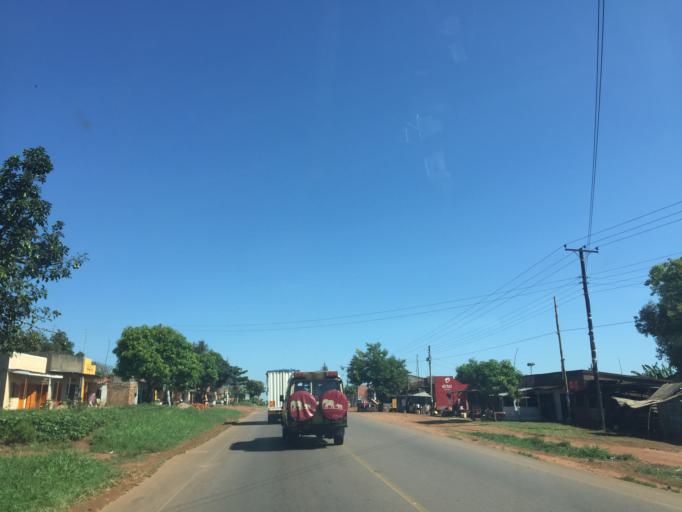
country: UG
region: Central Region
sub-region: Luwero District
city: Wobulenzi
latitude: 0.7497
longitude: 32.5157
